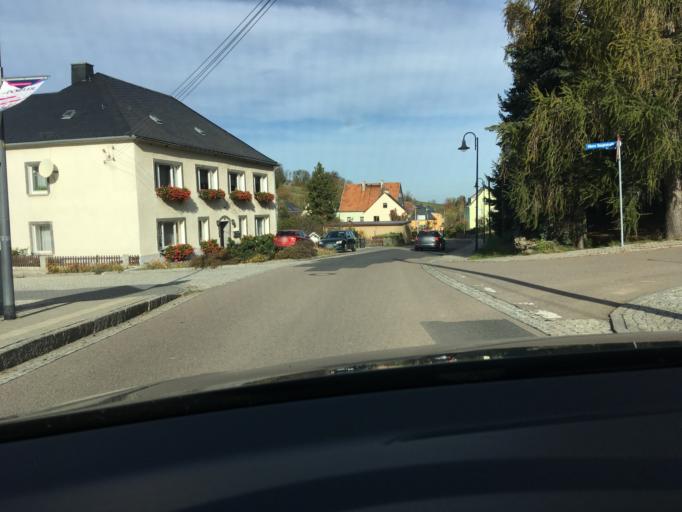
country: DE
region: Saxony
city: Barenstein
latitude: 50.8275
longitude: 13.8058
